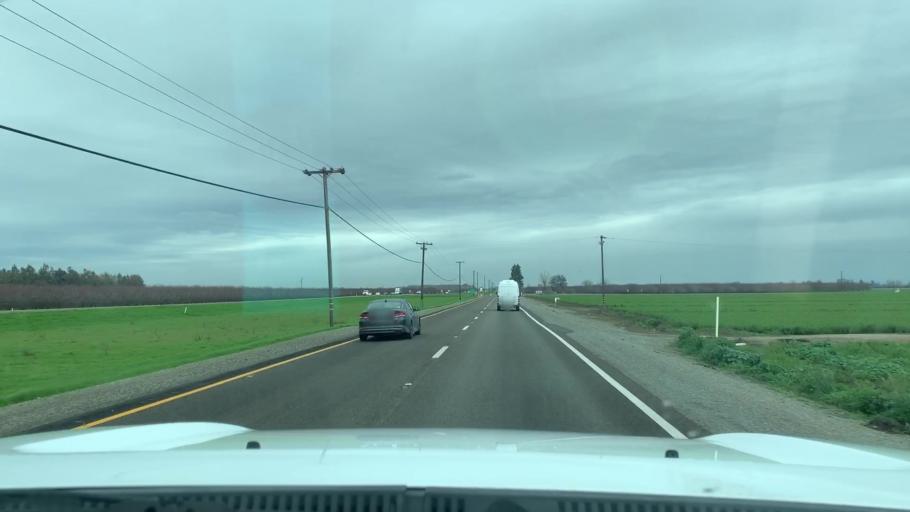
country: US
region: California
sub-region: Fresno County
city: Riverdale
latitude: 36.3764
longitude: -119.8096
